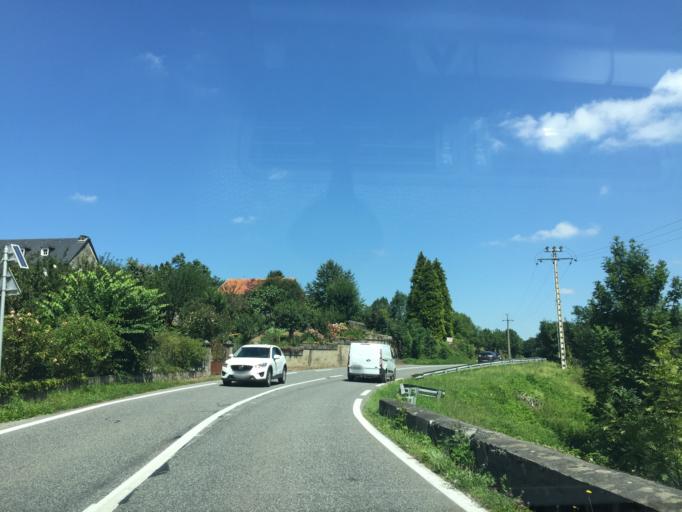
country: FR
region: Midi-Pyrenees
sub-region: Departement des Hautes-Pyrenees
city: La Barthe-de-Neste
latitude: 43.0148
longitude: 0.3726
